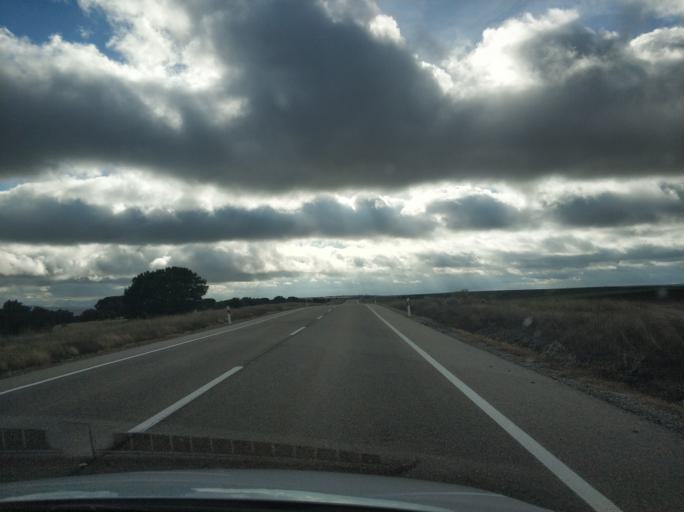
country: ES
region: Castille and Leon
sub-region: Provincia de Soria
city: Fuentecambron
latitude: 41.4813
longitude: -3.3177
